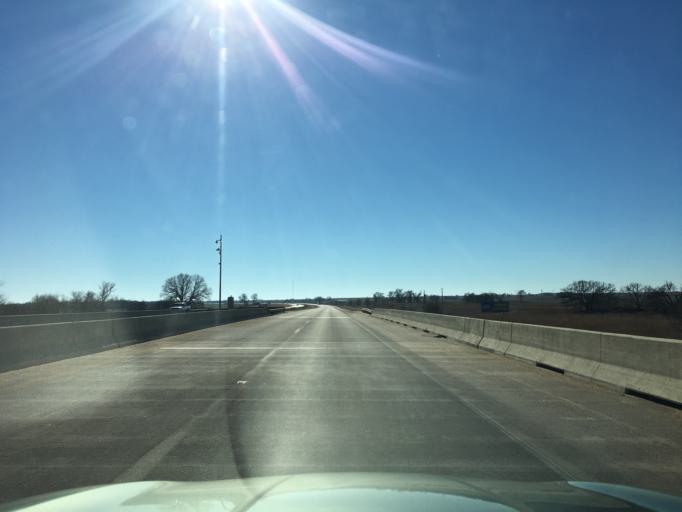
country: US
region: Oklahoma
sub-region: Kay County
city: Blackwell
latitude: 36.9075
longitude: -97.3531
